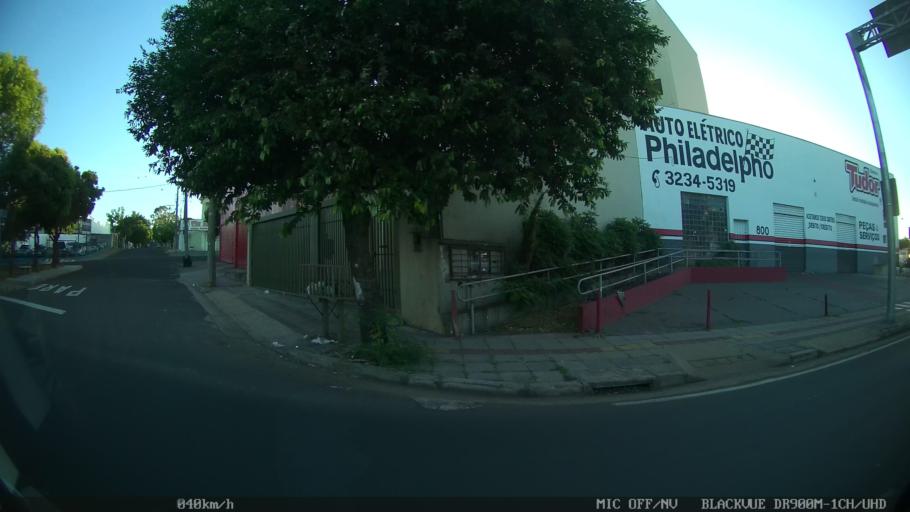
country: BR
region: Sao Paulo
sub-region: Sao Jose Do Rio Preto
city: Sao Jose do Rio Preto
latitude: -20.7871
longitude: -49.3774
